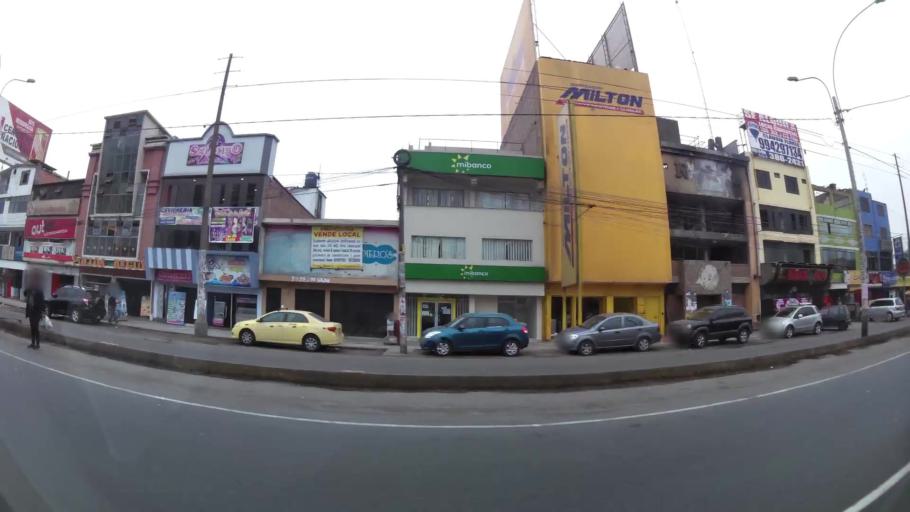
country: PE
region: Lima
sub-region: Lima
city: Independencia
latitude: -11.9342
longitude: -77.0473
